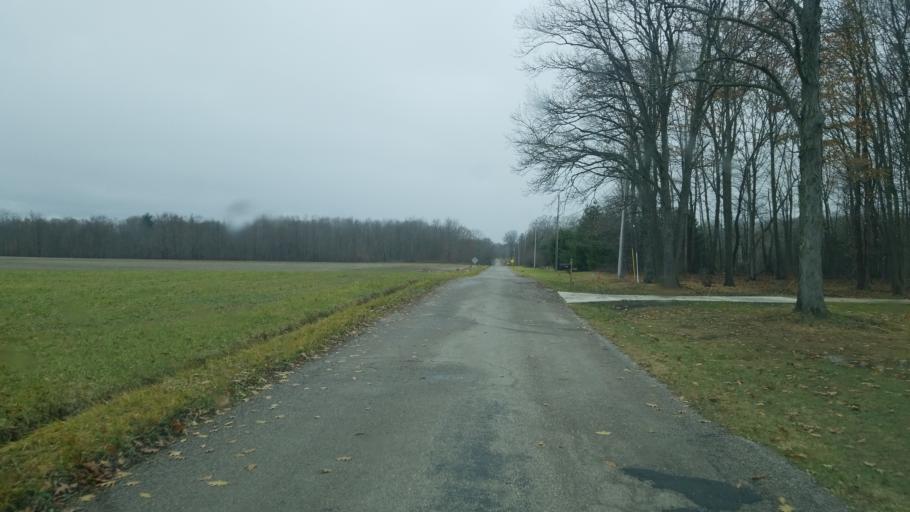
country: US
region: Ohio
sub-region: Ashtabula County
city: Jefferson
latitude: 41.7530
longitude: -80.8450
